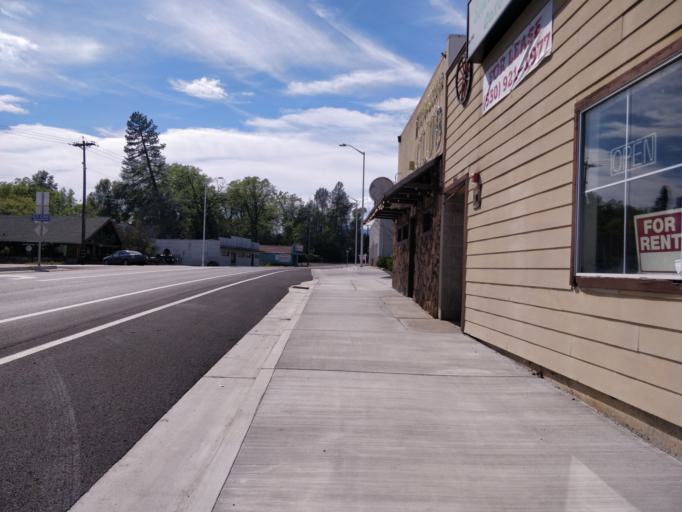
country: US
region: California
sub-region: Shasta County
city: Central Valley (historical)
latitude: 40.6812
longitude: -122.3716
